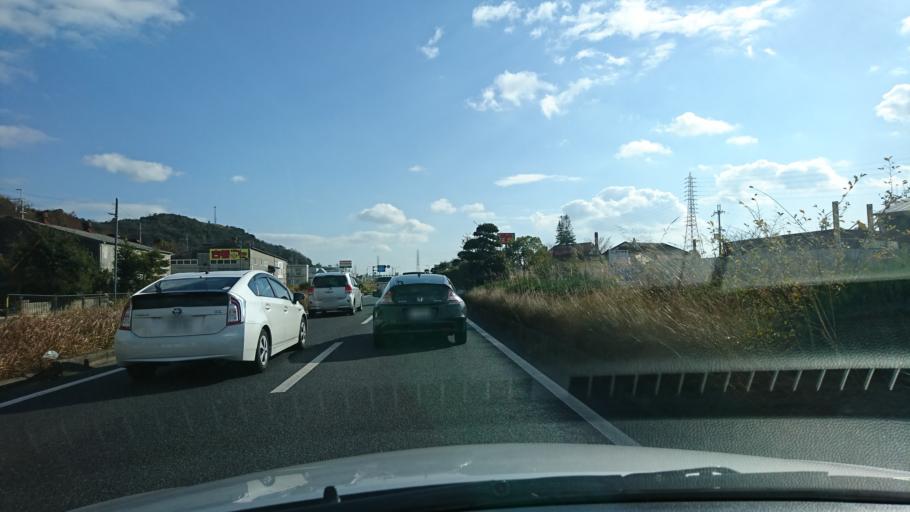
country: JP
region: Hyogo
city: Kakogawacho-honmachi
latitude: 34.7801
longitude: 134.7890
